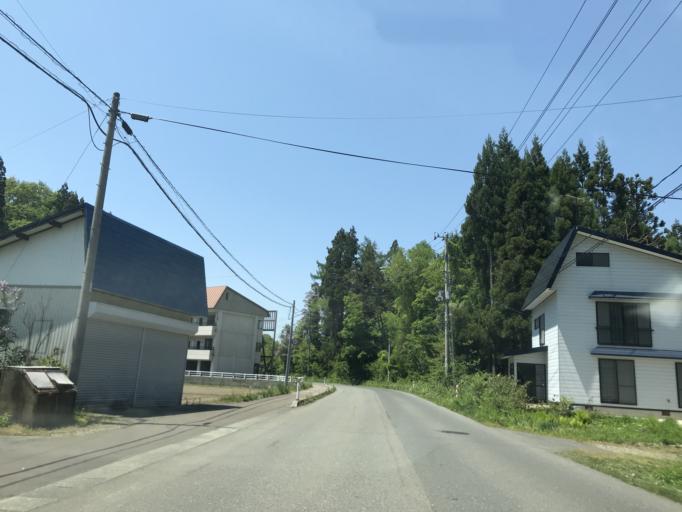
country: JP
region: Akita
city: Yokotemachi
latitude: 39.3555
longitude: 140.7669
